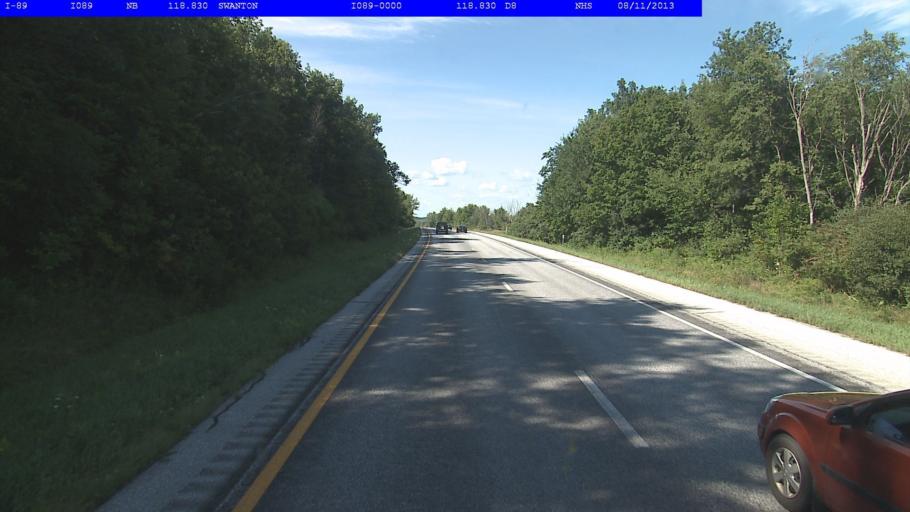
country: US
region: Vermont
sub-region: Franklin County
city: Saint Albans
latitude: 44.8602
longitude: -73.0804
